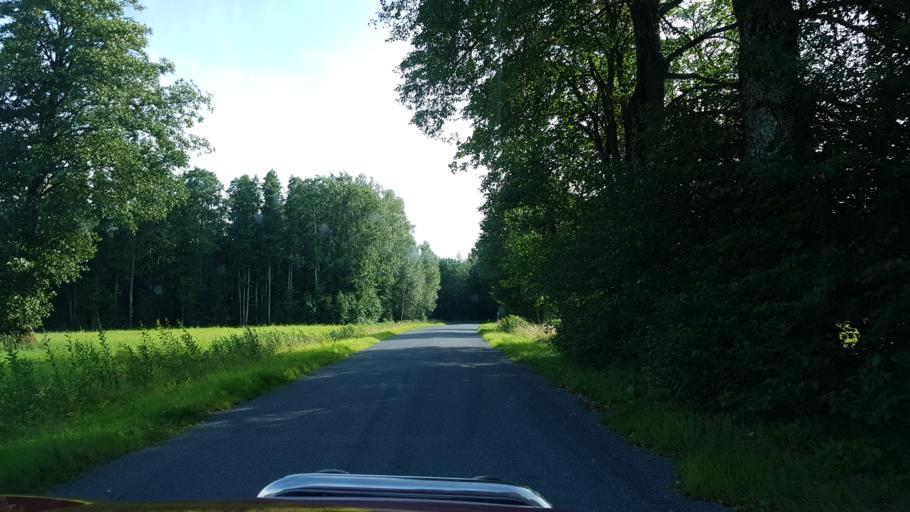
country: EE
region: Laeaene
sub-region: Lihula vald
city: Lihula
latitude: 58.4041
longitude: 24.0080
